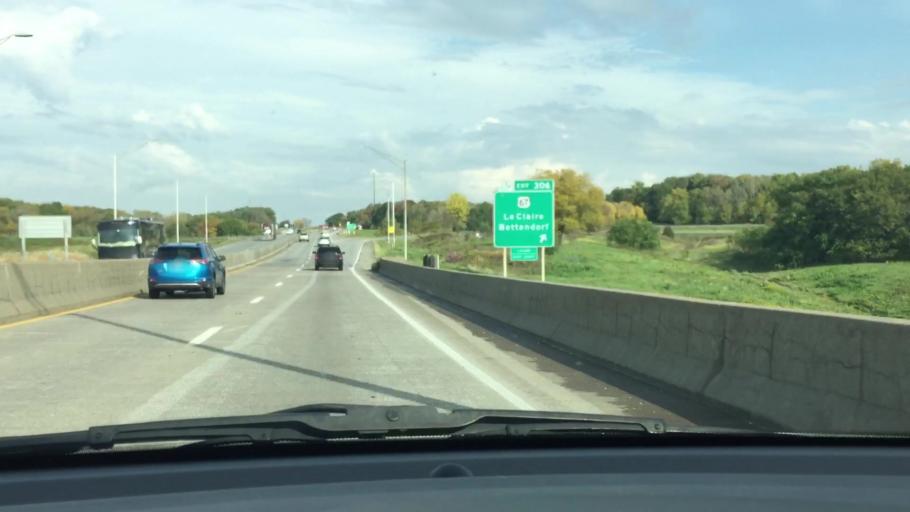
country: US
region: Iowa
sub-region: Scott County
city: Le Claire
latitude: 41.5841
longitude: -90.3673
